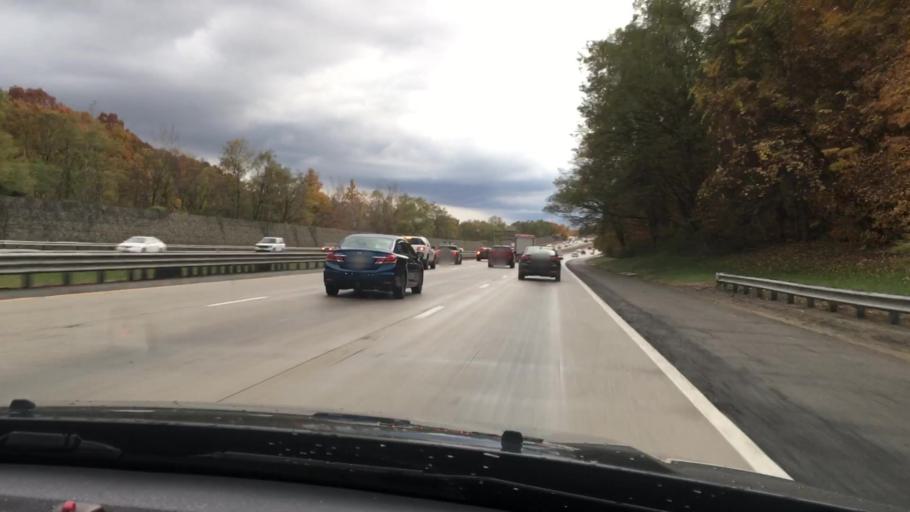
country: US
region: New Jersey
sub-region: Morris County
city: Riverdale
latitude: 40.9766
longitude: -74.3186
